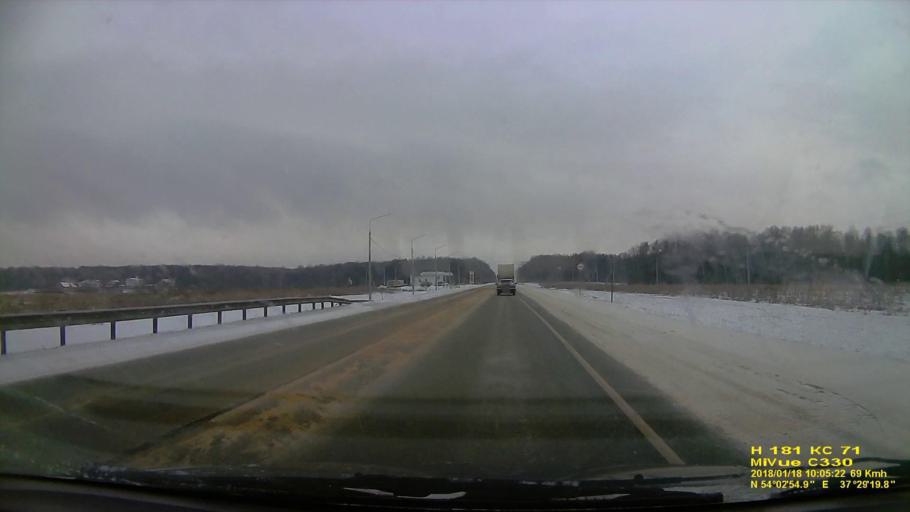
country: RU
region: Tula
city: Pervomayskiy
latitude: 54.0484
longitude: 37.4888
